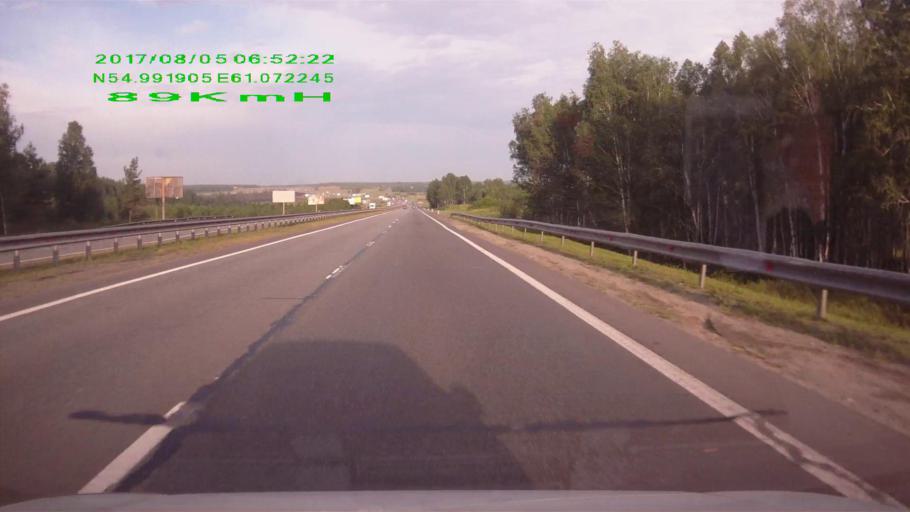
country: RU
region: Chelyabinsk
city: Poletayevo
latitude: 54.9919
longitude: 61.0714
